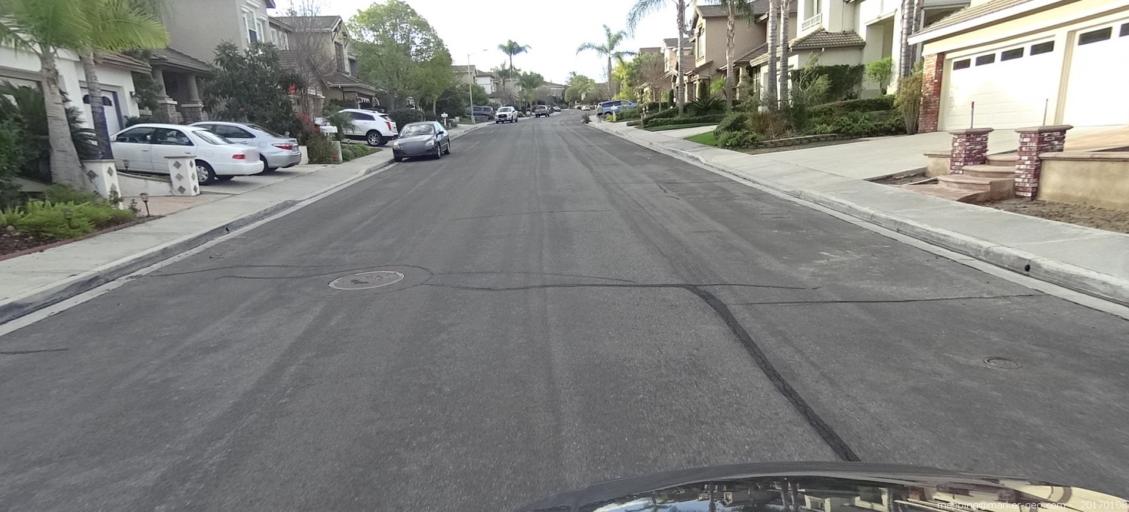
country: US
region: California
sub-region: Orange County
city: Las Flores
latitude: 33.5929
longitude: -117.6210
